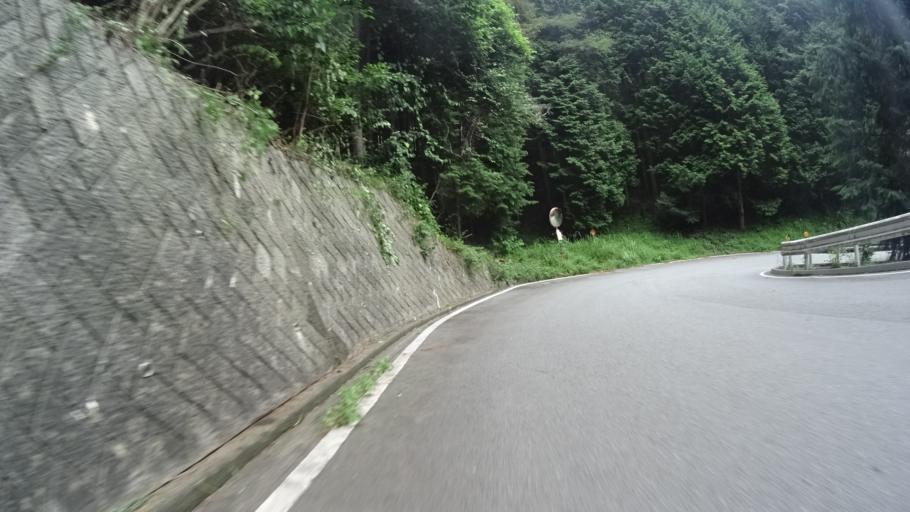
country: JP
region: Yamanashi
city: Enzan
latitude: 35.7915
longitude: 138.6834
